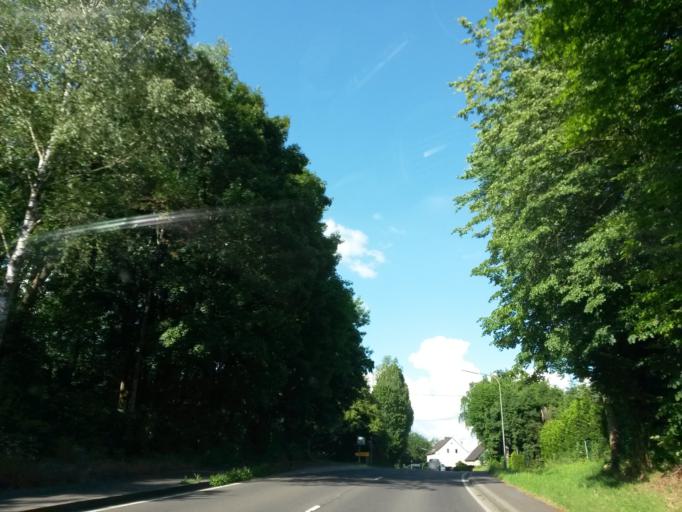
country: DE
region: North Rhine-Westphalia
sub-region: Regierungsbezirk Koln
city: Much
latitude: 50.9111
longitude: 7.4195
